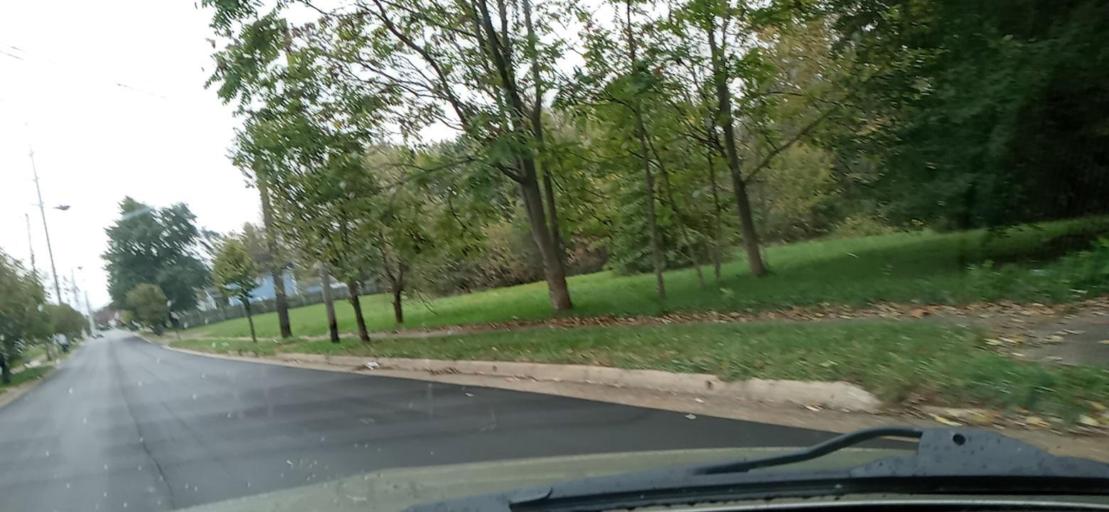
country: US
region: Ohio
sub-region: Summit County
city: Akron
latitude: 41.0535
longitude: -81.5415
